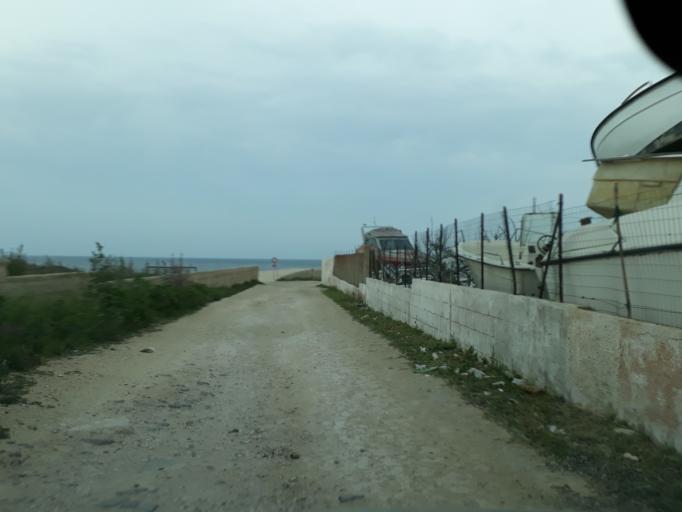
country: IT
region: Apulia
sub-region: Provincia di Brindisi
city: Ostuni
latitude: 40.7911
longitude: 17.5853
